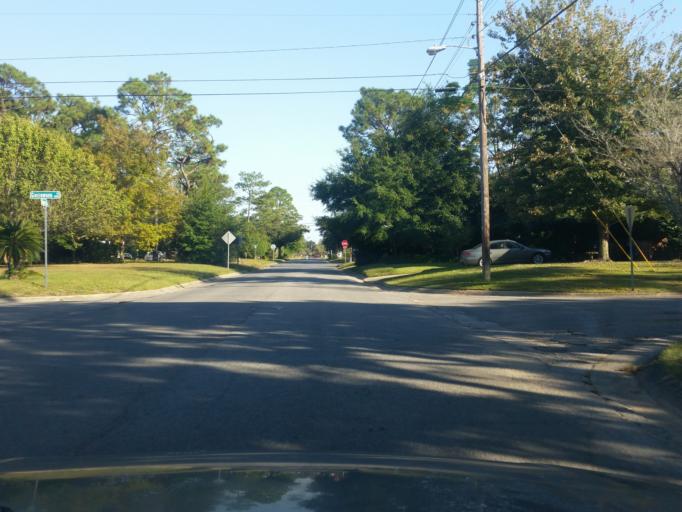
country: US
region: Florida
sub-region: Escambia County
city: Ferry Pass
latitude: 30.4932
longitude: -87.1816
